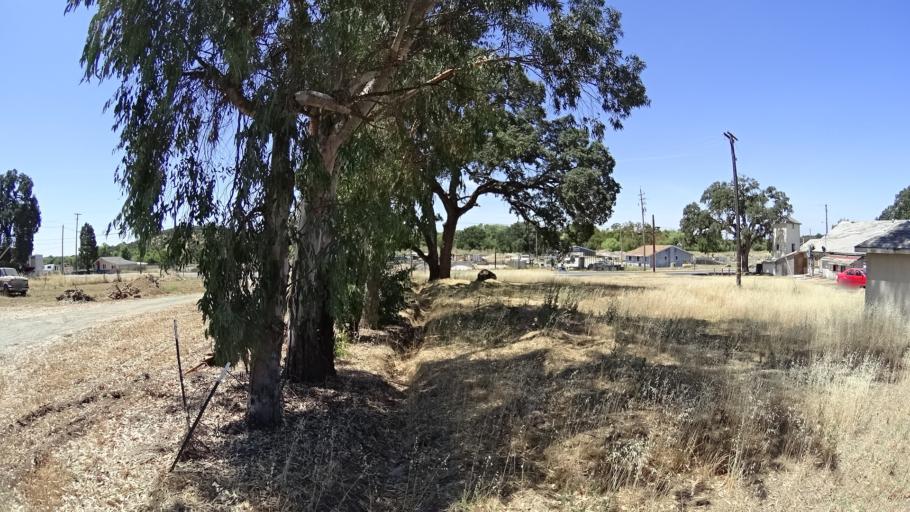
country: US
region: California
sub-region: San Joaquin County
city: Dogtown
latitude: 38.1942
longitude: -120.9766
